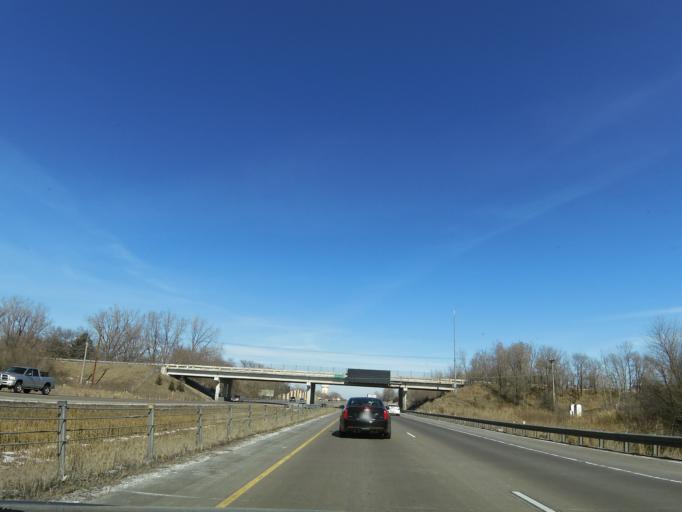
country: US
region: Minnesota
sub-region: Washington County
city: Oakdale
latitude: 44.9694
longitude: -92.9585
